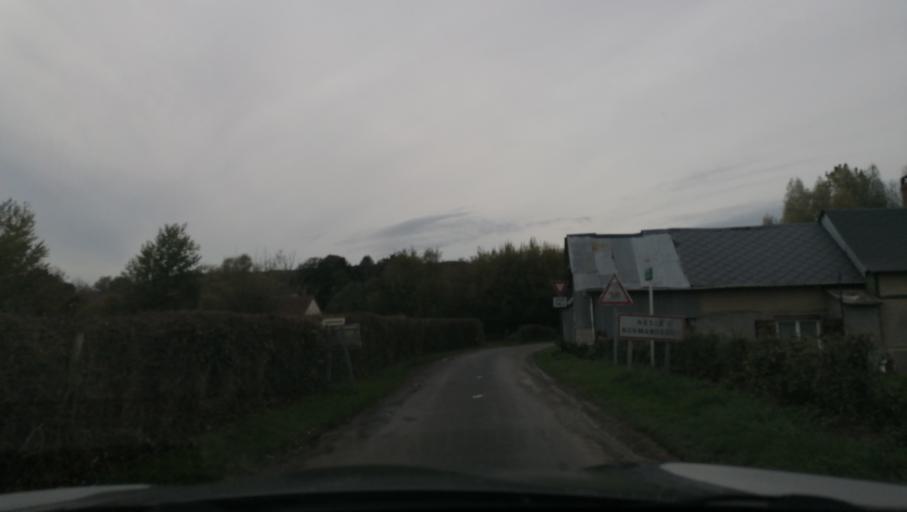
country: FR
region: Picardie
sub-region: Departement de la Somme
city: Bouttencourt
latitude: 49.9039
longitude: 1.6678
